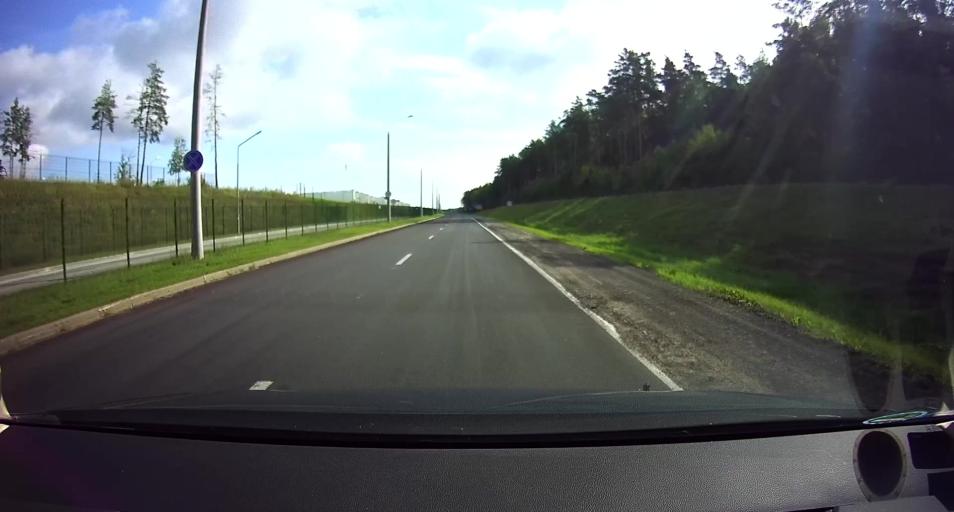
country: PL
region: Podlasie
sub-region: Powiat sokolski
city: Kuznica
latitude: 53.5247
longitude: 23.6713
